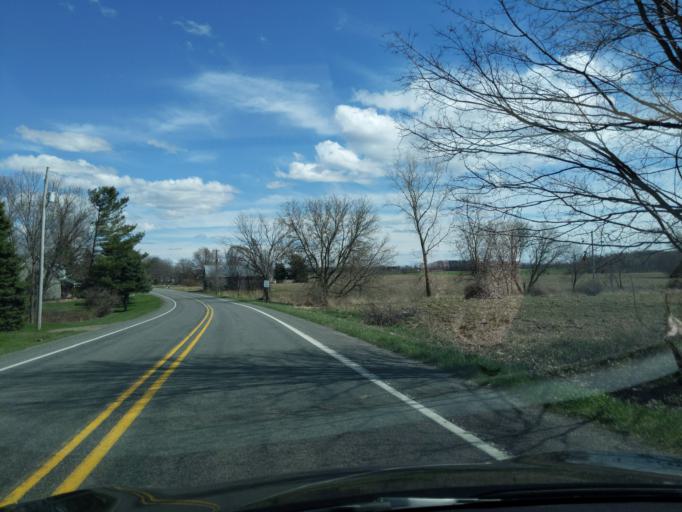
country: US
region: Michigan
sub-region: Ingham County
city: Mason
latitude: 42.5561
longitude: -84.4018
